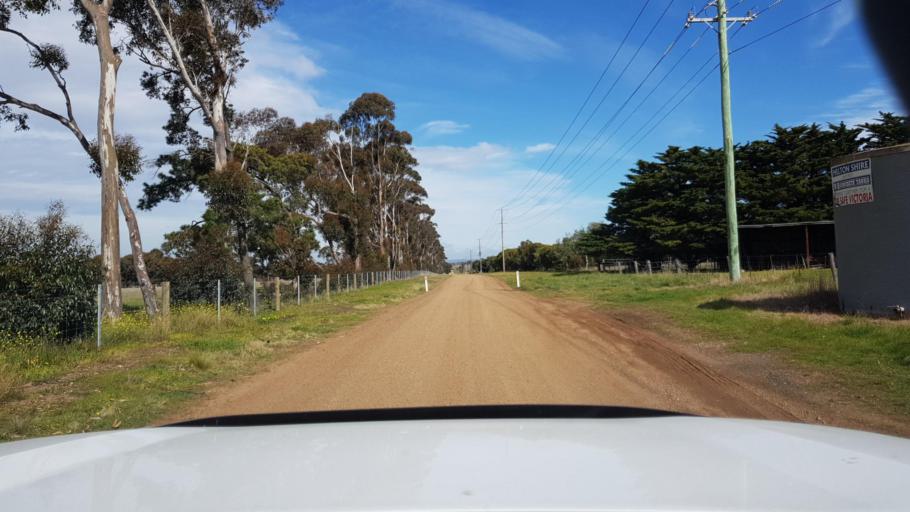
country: AU
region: Victoria
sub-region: Hume
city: Diggers Rest
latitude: -37.5984
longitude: 144.6744
